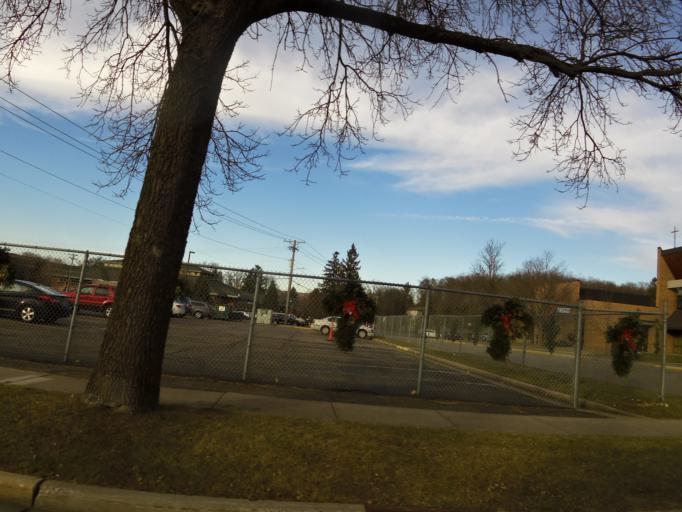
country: US
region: Wisconsin
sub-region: Pierce County
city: River Falls
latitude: 44.8626
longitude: -92.6220
